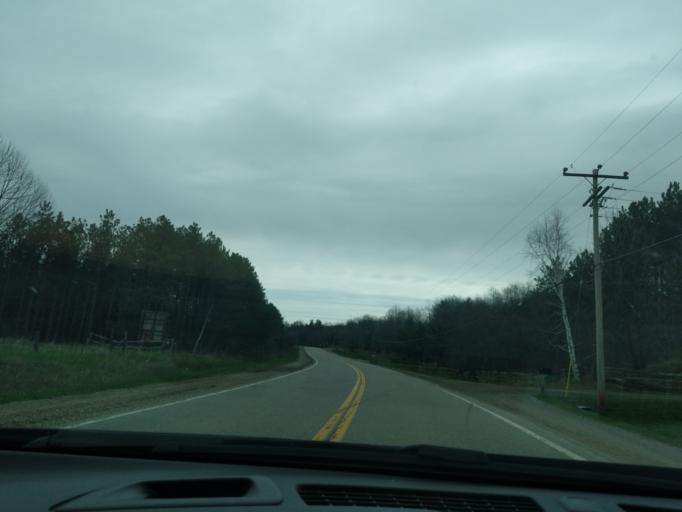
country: CA
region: Ontario
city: Orangeville
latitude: 43.9963
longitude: -80.0069
